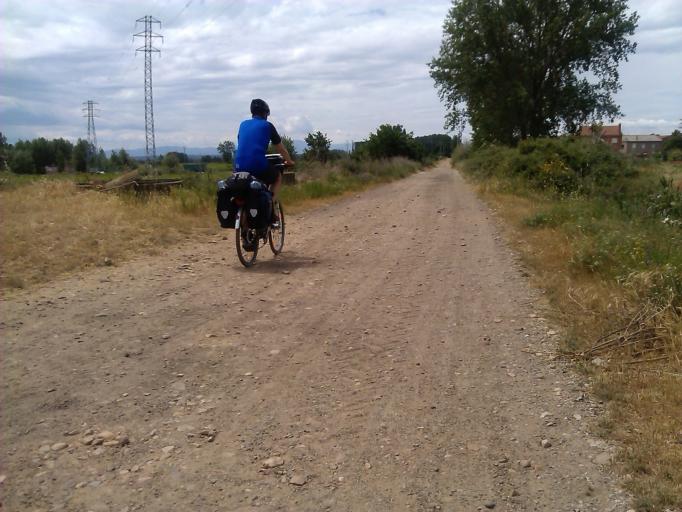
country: ES
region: Castille and Leon
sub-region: Provincia de Leon
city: Bustillo del Paramo
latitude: 42.4601
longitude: -5.8322
